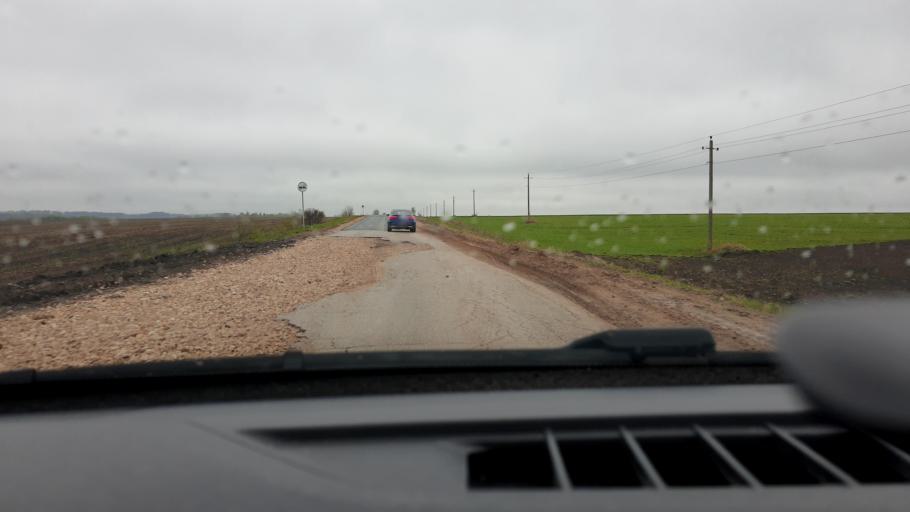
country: RU
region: Nizjnij Novgorod
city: Dal'neye Konstantinovo
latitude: 55.7663
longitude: 44.2500
